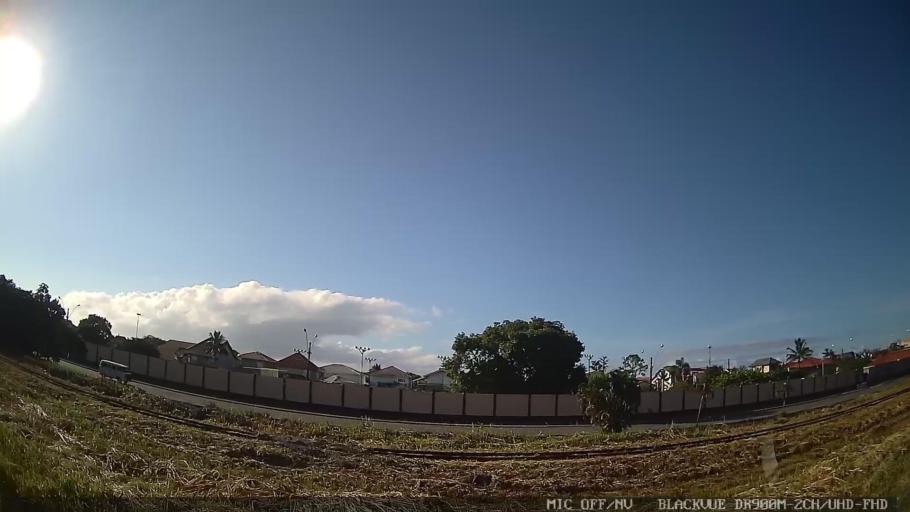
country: BR
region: Sao Paulo
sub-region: Peruibe
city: Peruibe
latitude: -24.2793
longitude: -46.9580
